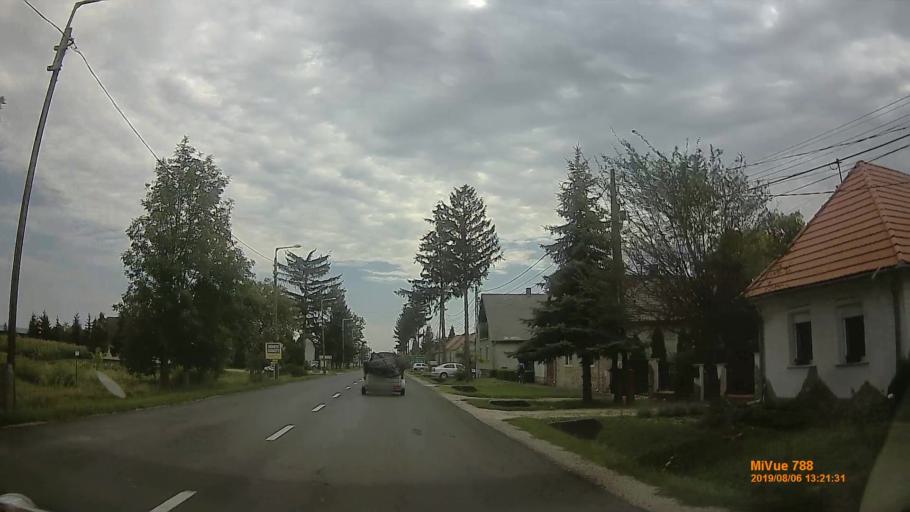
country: HU
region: Vas
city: Koszeg
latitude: 47.3430
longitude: 16.5774
